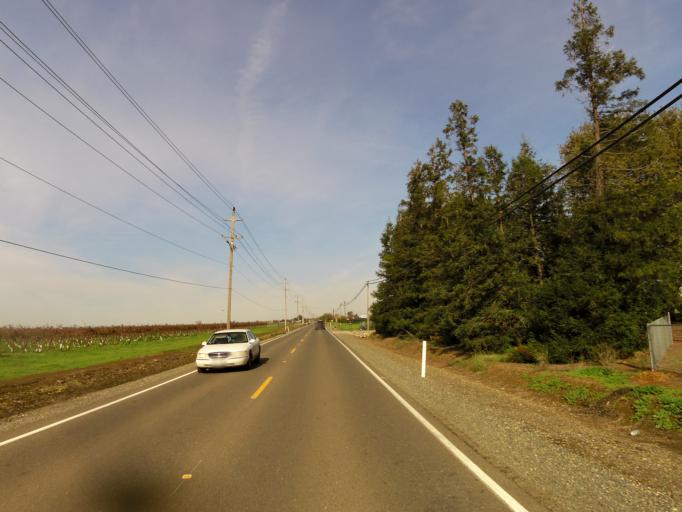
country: US
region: California
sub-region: Sacramento County
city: Laguna
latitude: 38.3628
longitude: -121.4175
